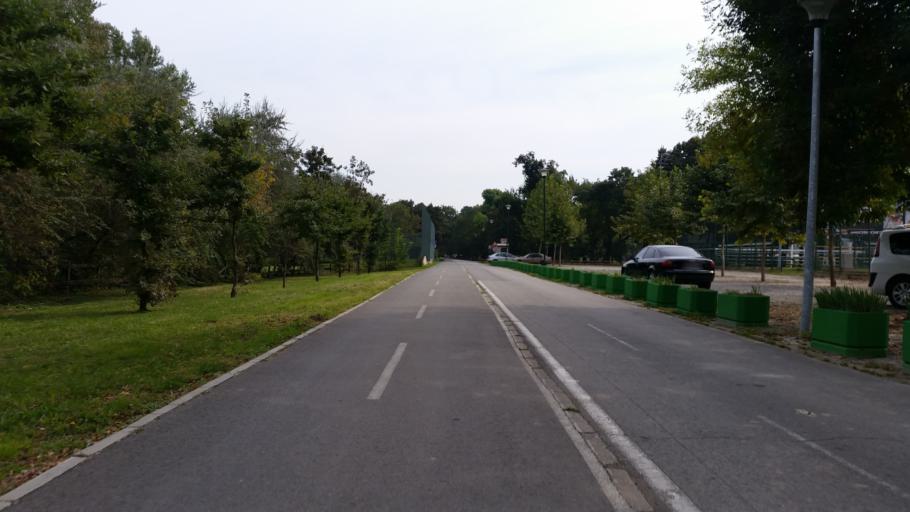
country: RS
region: Central Serbia
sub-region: Belgrade
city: Cukarica
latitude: 44.7884
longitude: 20.3999
